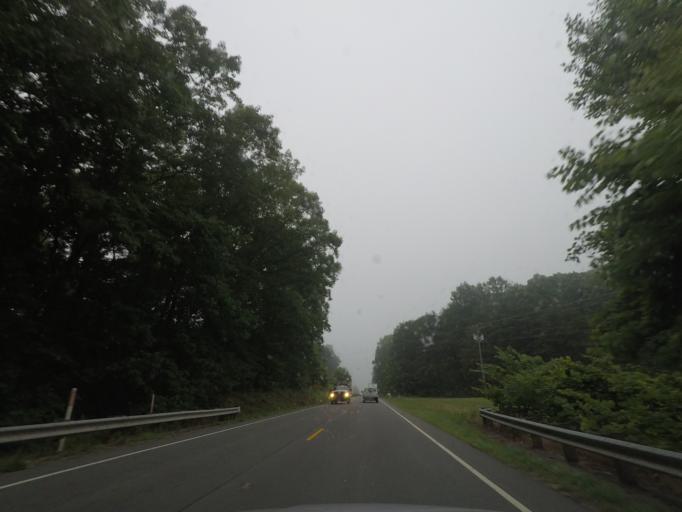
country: US
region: Virginia
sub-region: Buckingham County
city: Buckingham
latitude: 37.4684
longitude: -78.4703
